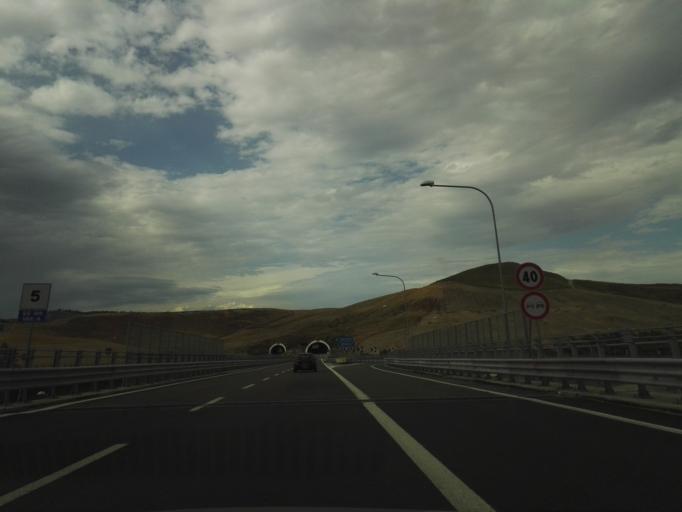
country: IT
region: Calabria
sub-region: Provincia di Catanzaro
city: Roccelletta
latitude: 38.8216
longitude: 16.5623
